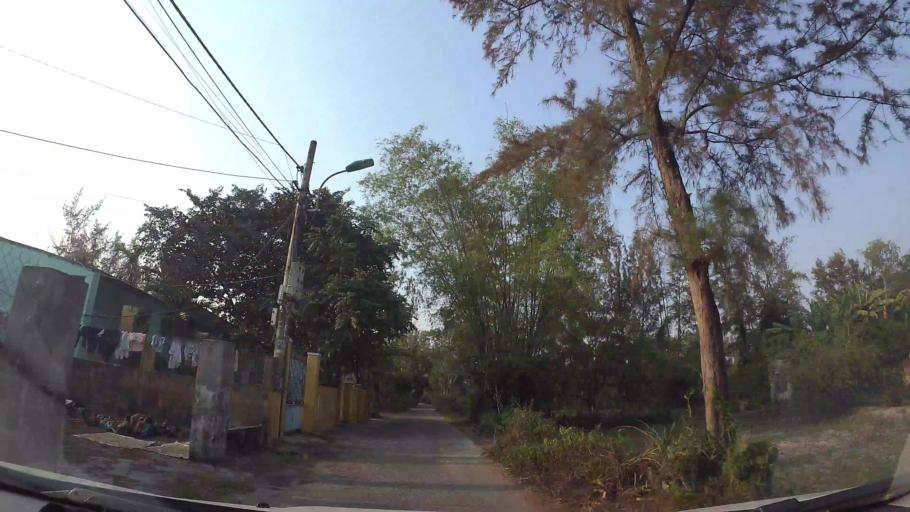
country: VN
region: Da Nang
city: Ngu Hanh Son
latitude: 15.9716
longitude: 108.2439
